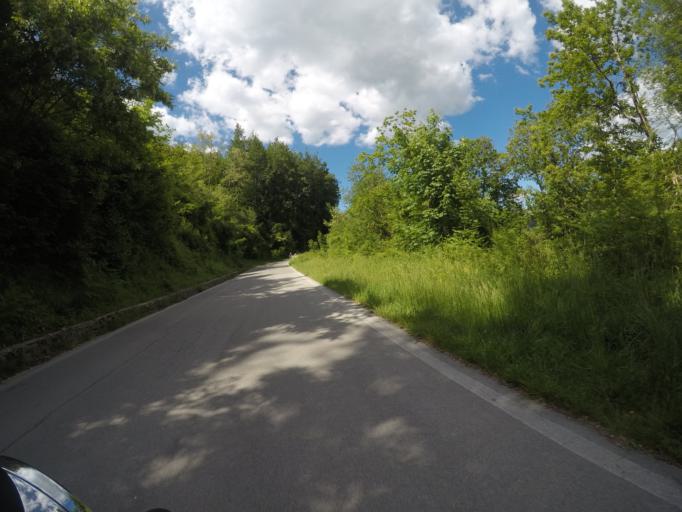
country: IT
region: Tuscany
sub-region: Provincia di Lucca
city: Minucciano
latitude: 44.1647
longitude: 10.2010
